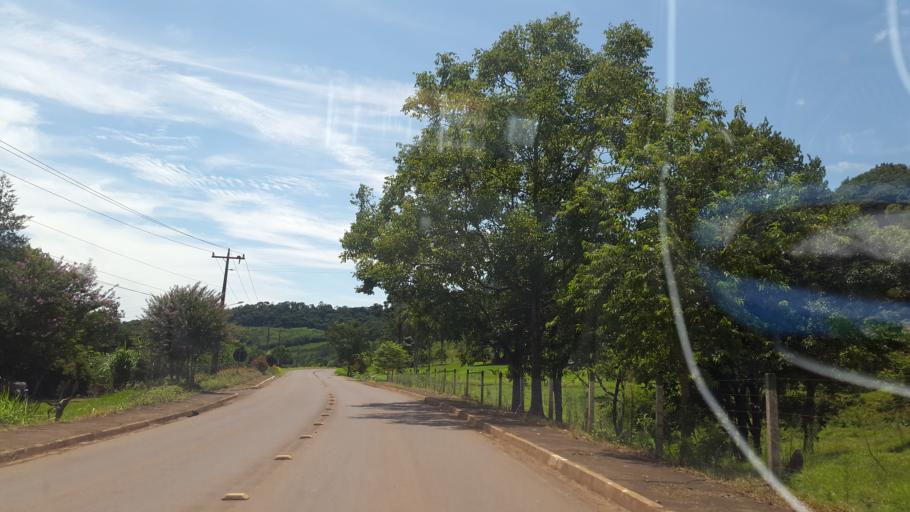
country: BR
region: Rio Grande do Sul
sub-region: Frederico Westphalen
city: Frederico Westphalen
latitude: -27.0698
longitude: -53.4494
